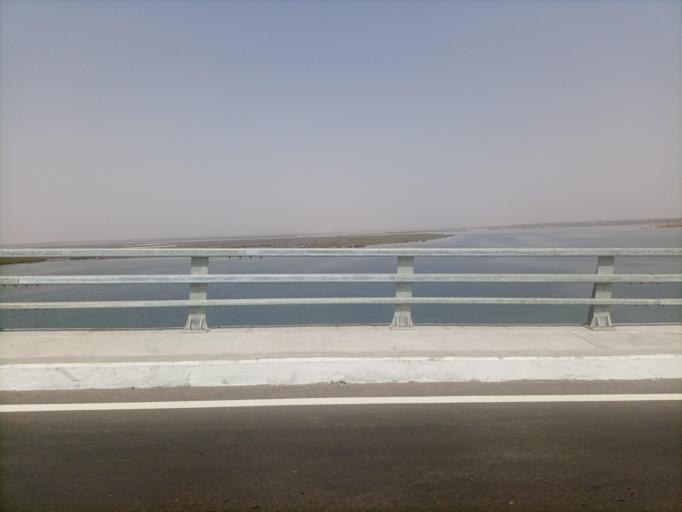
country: SN
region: Fatick
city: Foundiougne
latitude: 14.1353
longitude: -16.4684
